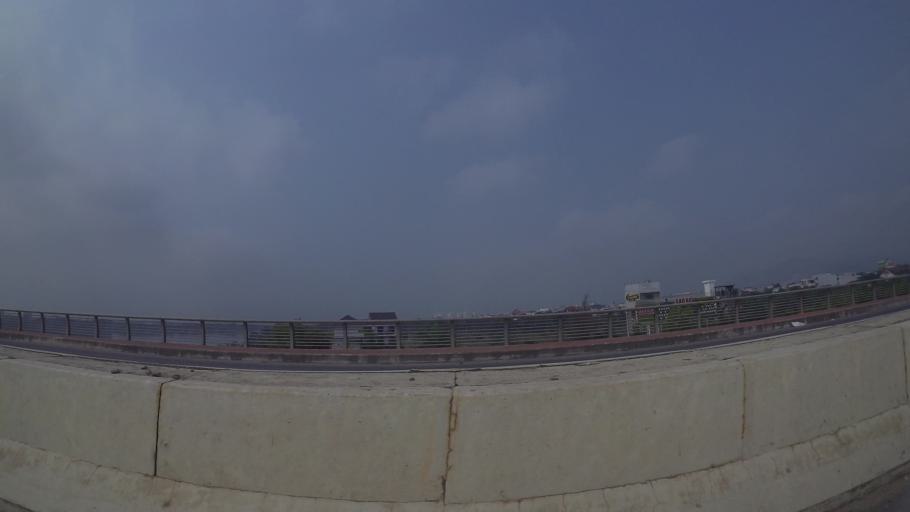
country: VN
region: Da Nang
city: Cam Le
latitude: 16.0165
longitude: 108.2134
